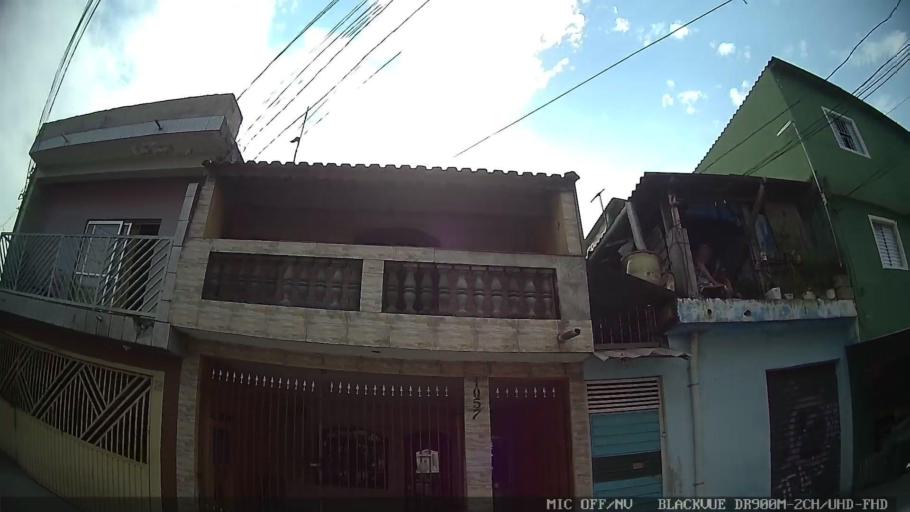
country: BR
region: Sao Paulo
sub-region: Ferraz De Vasconcelos
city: Ferraz de Vasconcelos
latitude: -23.4994
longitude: -46.4152
